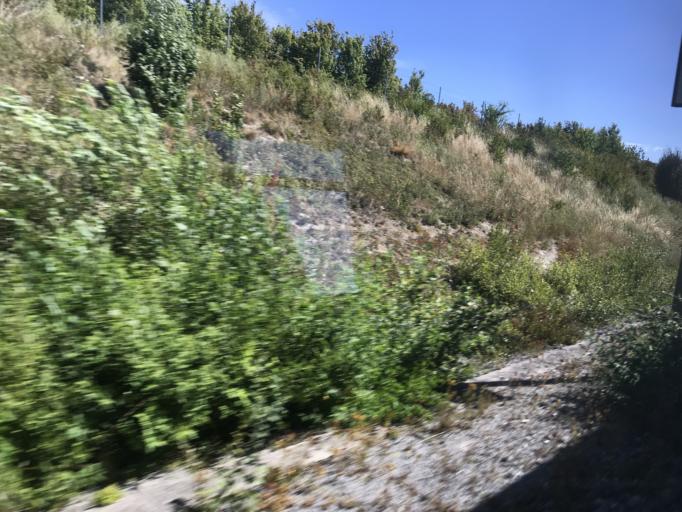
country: FR
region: Champagne-Ardenne
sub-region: Departement de la Marne
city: Cormontreuil
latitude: 49.2061
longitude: 4.0184
